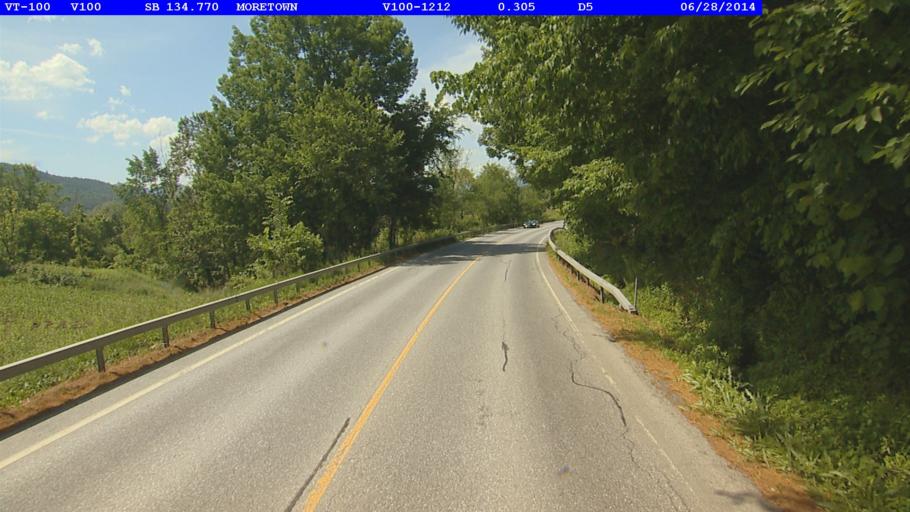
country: US
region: Vermont
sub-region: Washington County
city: Waterbury
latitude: 44.2382
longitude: -72.7760
